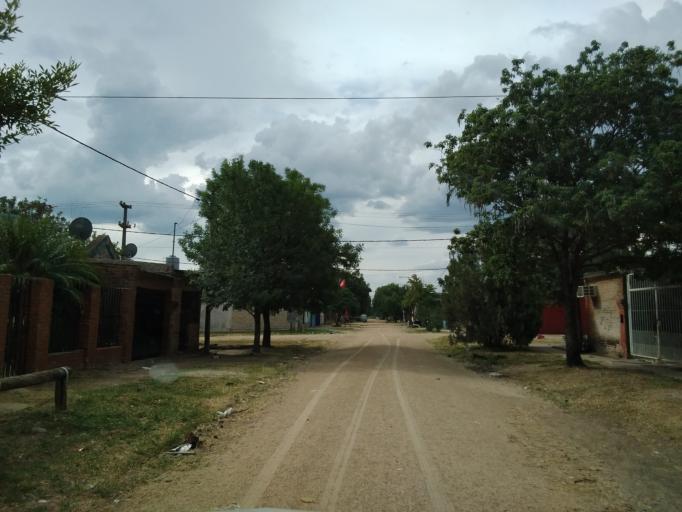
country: AR
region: Corrientes
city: Corrientes
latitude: -27.5215
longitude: -58.7924
